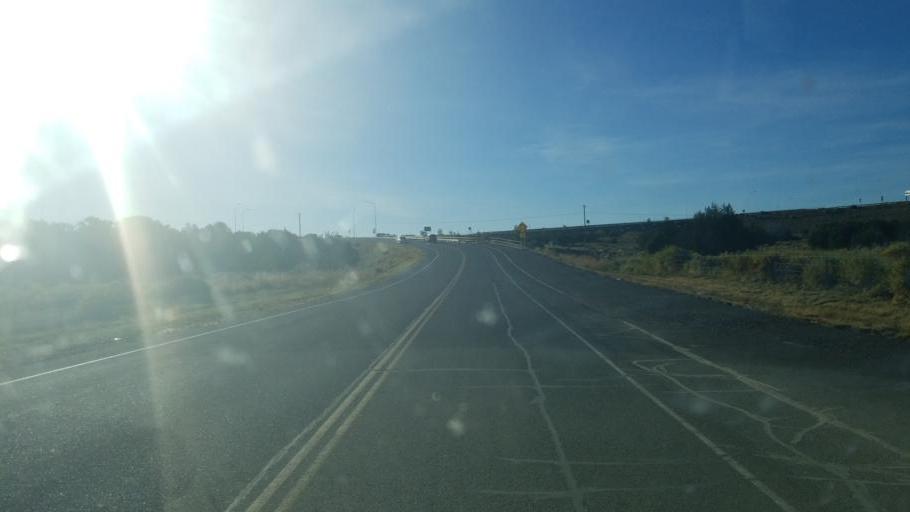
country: US
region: New Mexico
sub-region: Cibola County
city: Skyline-Ganipa
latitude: 35.0717
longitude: -107.5572
